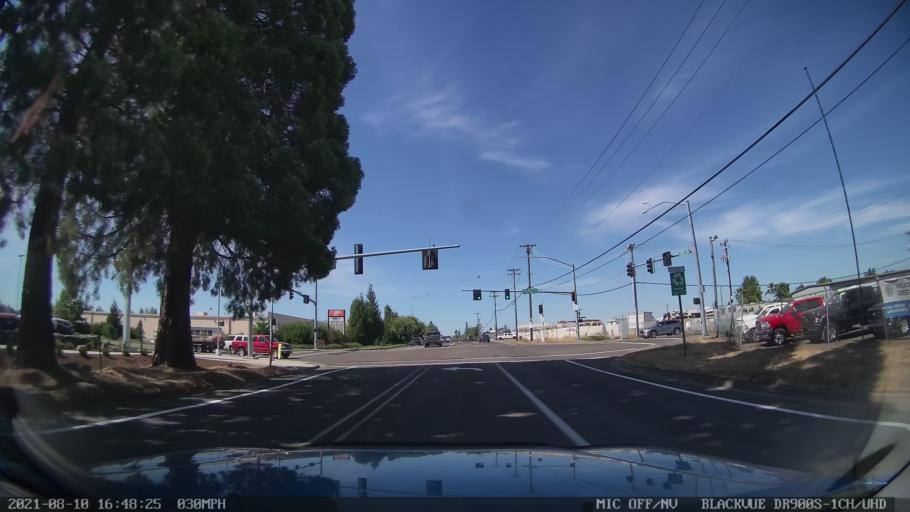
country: US
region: Oregon
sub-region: Marion County
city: Keizer
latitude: 44.9692
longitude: -123.0200
